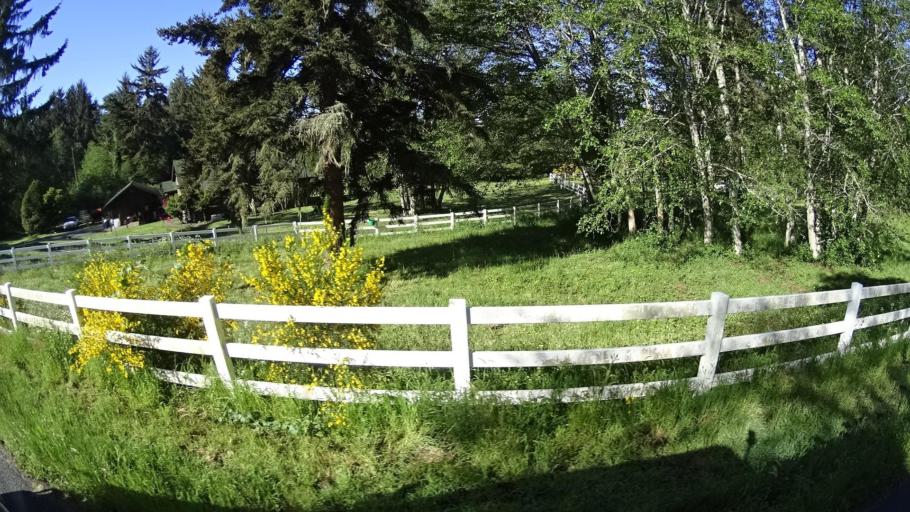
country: US
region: California
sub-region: Humboldt County
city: Westhaven-Moonstone
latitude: 40.9964
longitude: -124.0998
